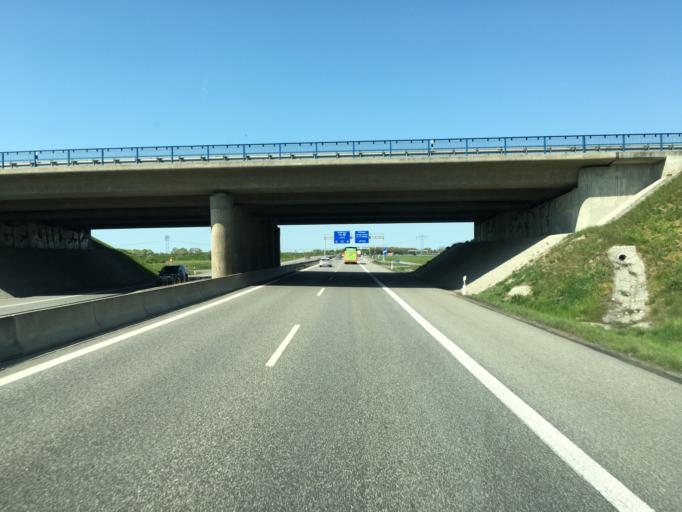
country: DE
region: Saxony
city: Borsdorf
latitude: 51.3108
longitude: 12.5549
